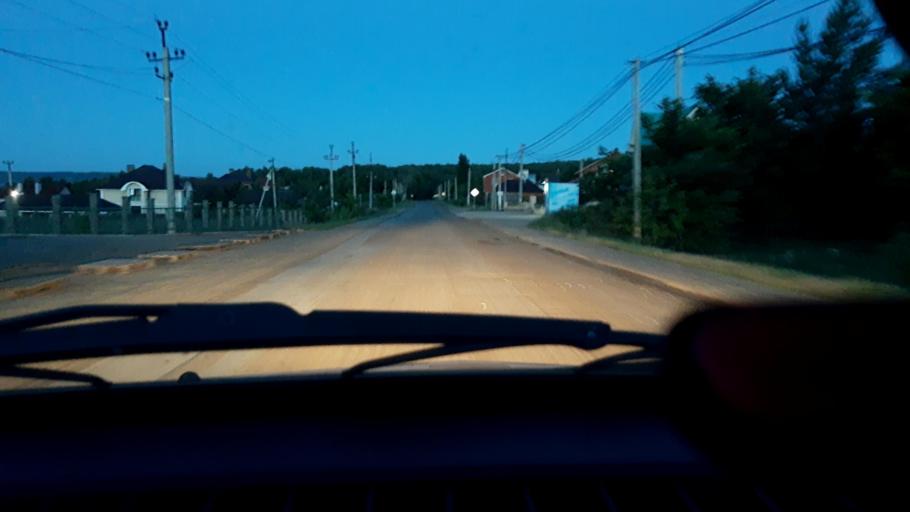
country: RU
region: Bashkortostan
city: Avdon
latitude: 54.6432
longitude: 55.7038
